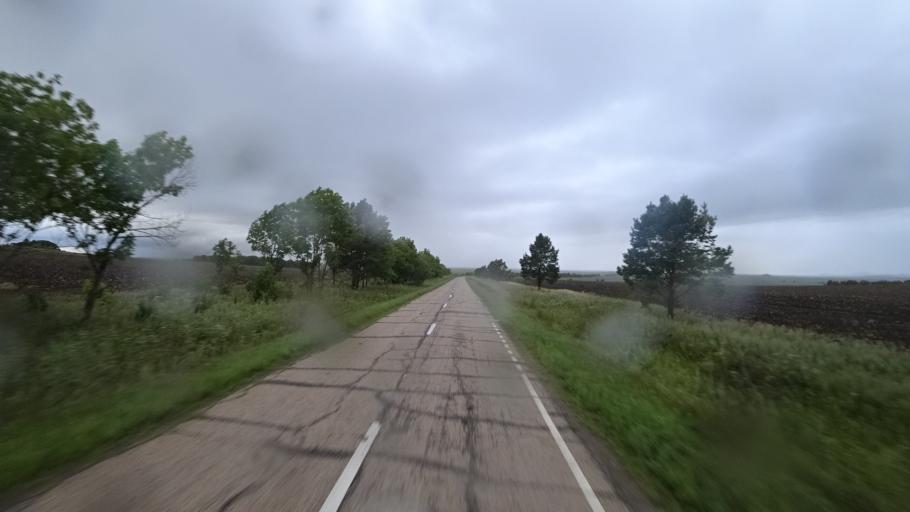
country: RU
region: Primorskiy
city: Chernigovka
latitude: 44.3684
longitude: 132.5328
